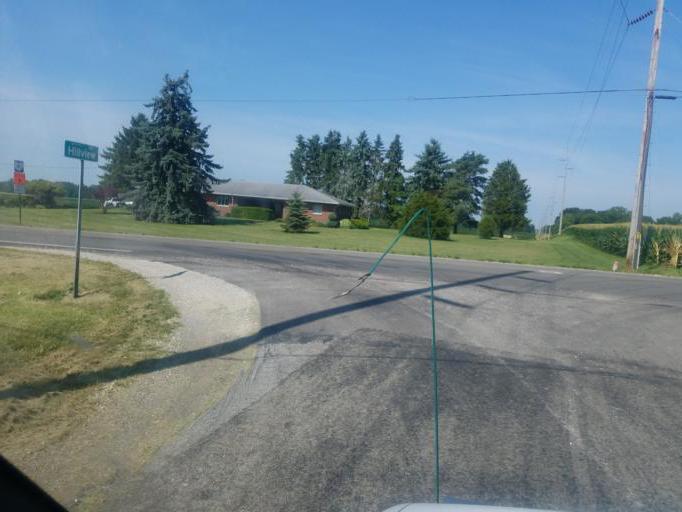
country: US
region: Ohio
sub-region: Union County
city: Marysville
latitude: 40.2870
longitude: -83.3778
